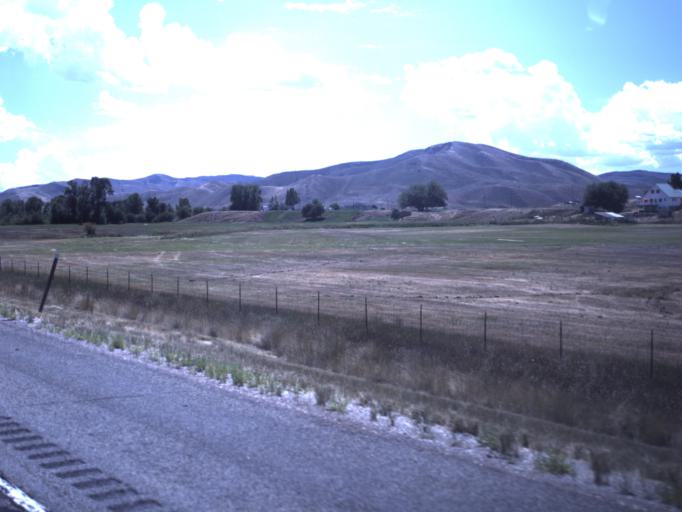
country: US
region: Utah
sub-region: Morgan County
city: Morgan
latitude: 41.0386
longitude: -111.5143
